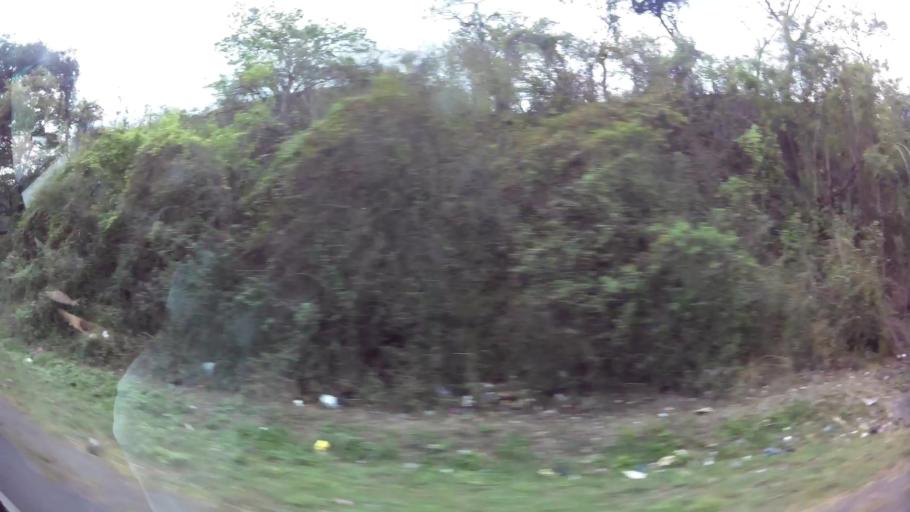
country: NI
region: Matagalpa
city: Matagalpa
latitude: 12.9151
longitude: -85.9408
